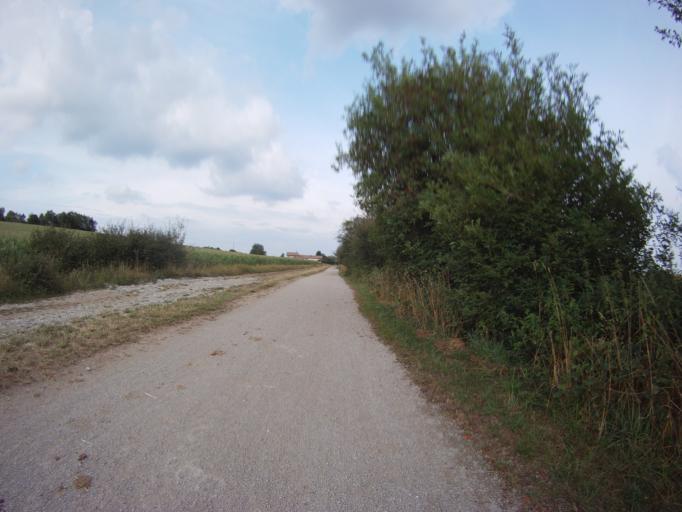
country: FR
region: Lorraine
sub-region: Departement de la Moselle
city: Mecleuves
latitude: 49.0729
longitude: 6.3235
